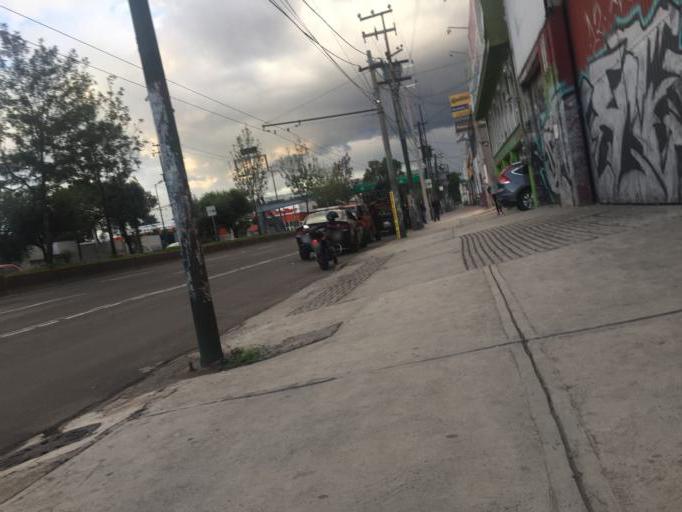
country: MX
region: Mexico City
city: Iztapalapa
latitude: 19.3550
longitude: -99.0839
